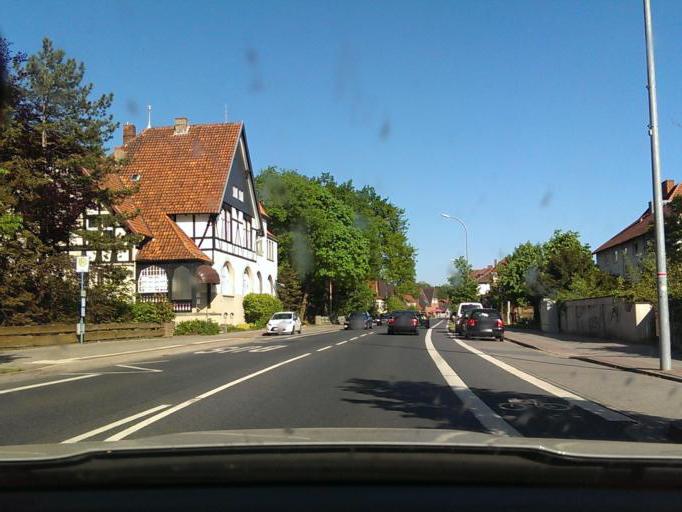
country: DE
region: Lower Saxony
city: Wietze
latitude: 52.6563
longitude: 9.8354
